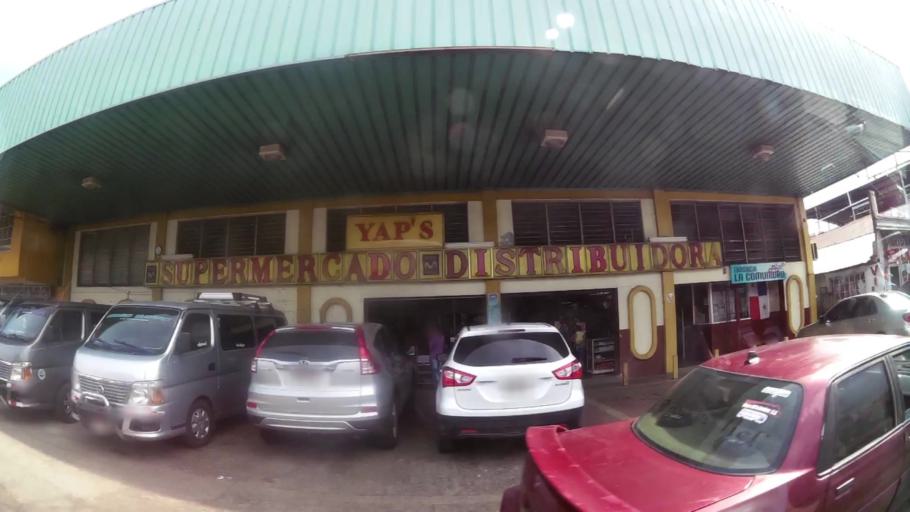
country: PA
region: Panama
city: La Chorrera
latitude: 8.8768
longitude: -79.7862
